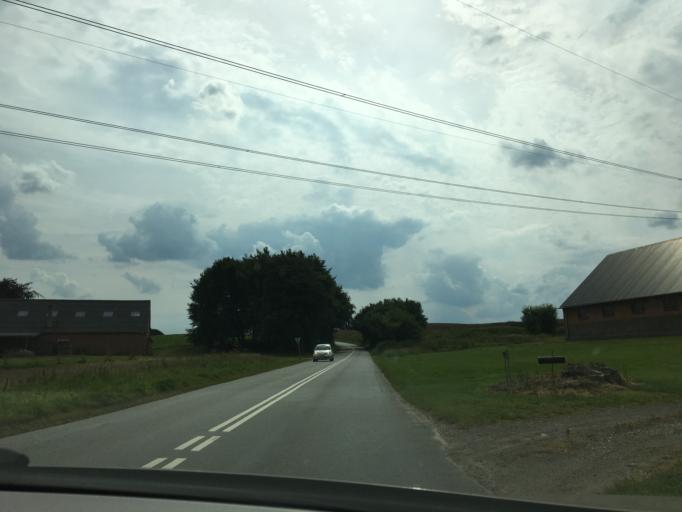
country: DK
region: Central Jutland
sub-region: Viborg Kommune
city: Stoholm
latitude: 56.4715
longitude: 9.1473
